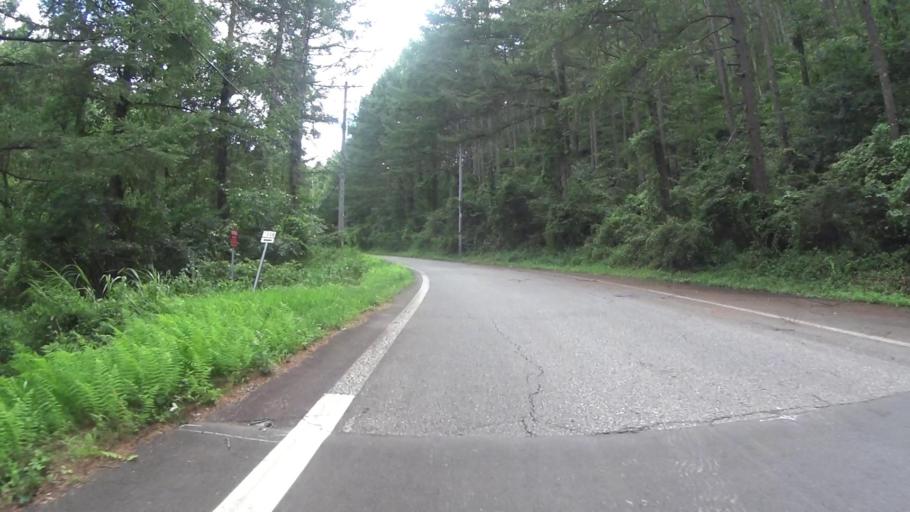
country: JP
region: Nagano
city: Saku
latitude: 36.1611
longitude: 138.3922
